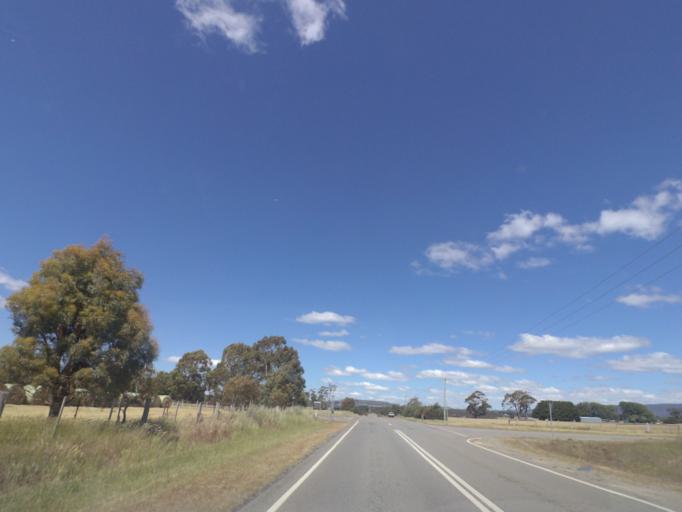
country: AU
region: Victoria
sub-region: Mount Alexander
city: Castlemaine
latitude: -37.2911
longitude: 144.4876
